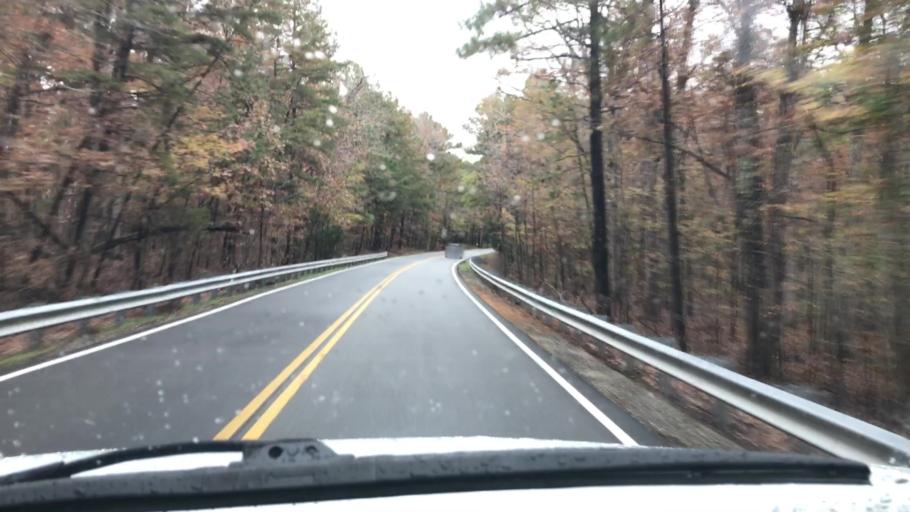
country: US
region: Virginia
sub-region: Henrico County
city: Short Pump
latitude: 37.6057
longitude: -77.6985
